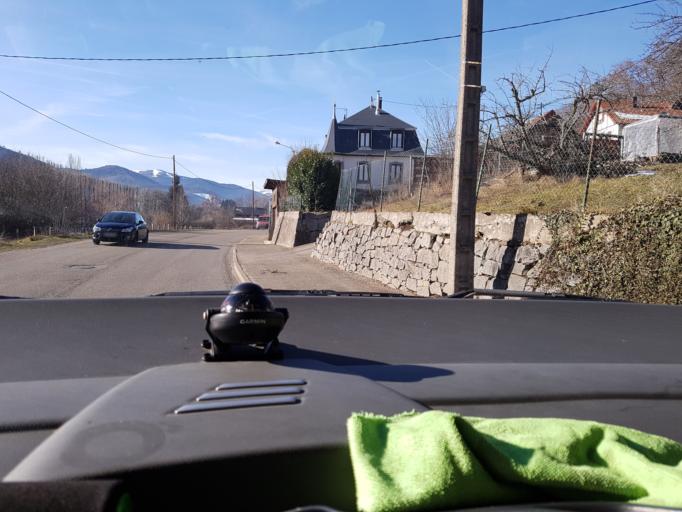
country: FR
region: Alsace
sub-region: Departement du Haut-Rhin
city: Munster
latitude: 48.0382
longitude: 7.1253
